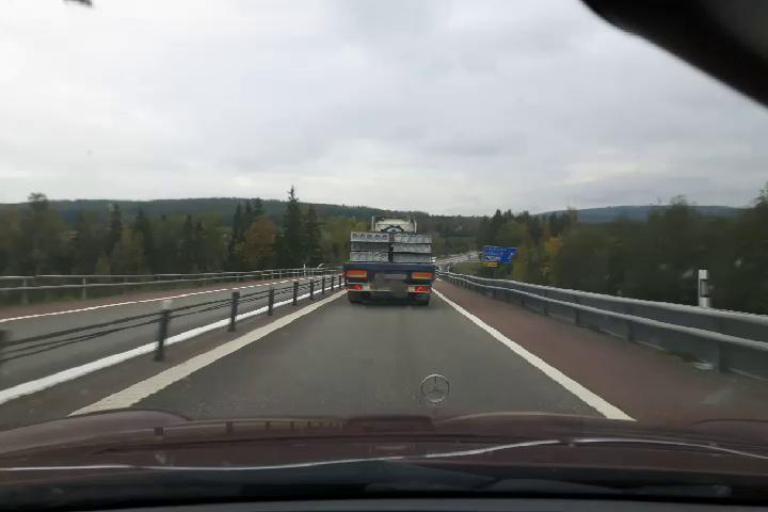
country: SE
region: Vaesternorrland
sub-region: Haernoesands Kommun
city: Haernoesand
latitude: 62.7712
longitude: 17.9156
